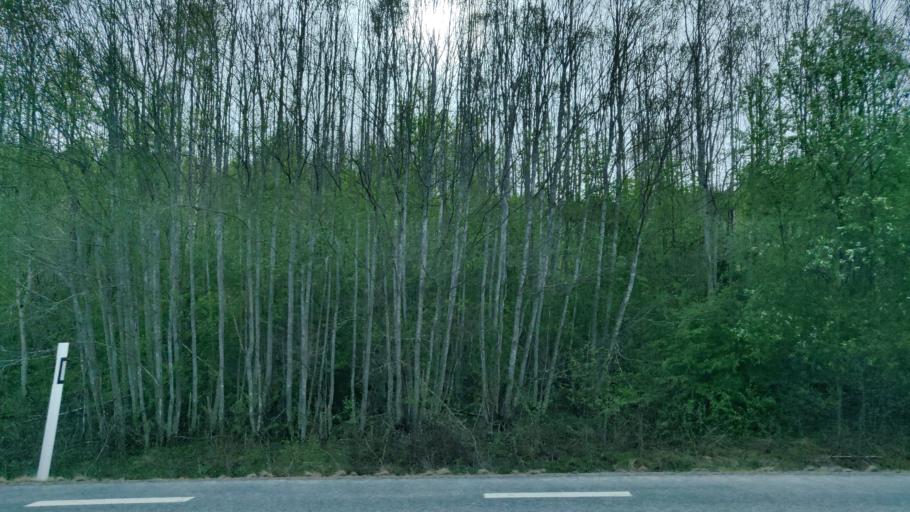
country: SE
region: Vaermland
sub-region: Munkfors Kommun
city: Munkfors
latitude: 59.7656
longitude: 13.4396
